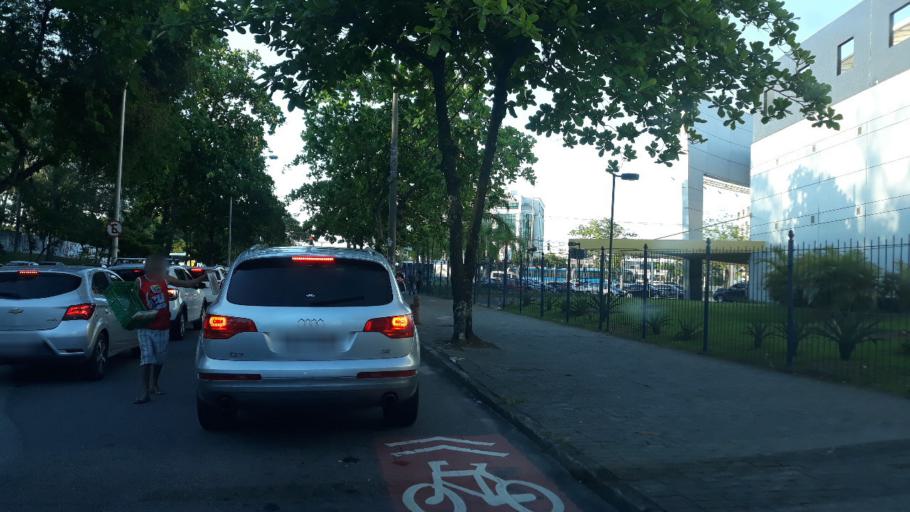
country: BR
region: Rio de Janeiro
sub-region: Rio De Janeiro
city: Rio de Janeiro
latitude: -23.0013
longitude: -43.3532
